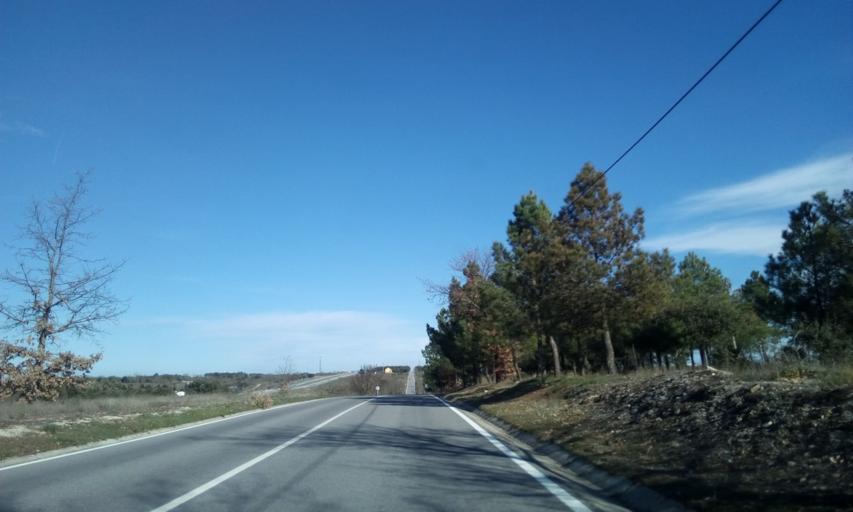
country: ES
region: Castille and Leon
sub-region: Provincia de Salamanca
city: Fuentes de Onoro
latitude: 40.6146
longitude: -6.8773
